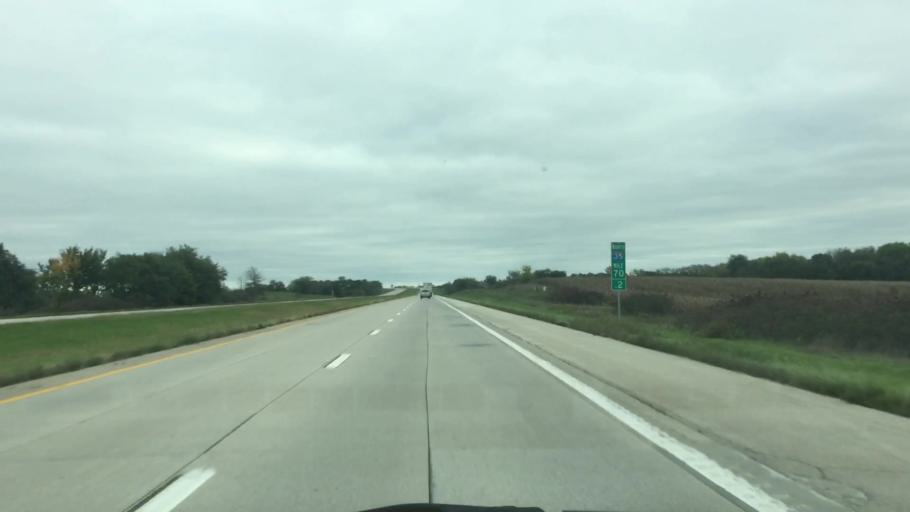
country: US
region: Missouri
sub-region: Daviess County
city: Gallatin
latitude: 39.9640
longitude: -94.1009
